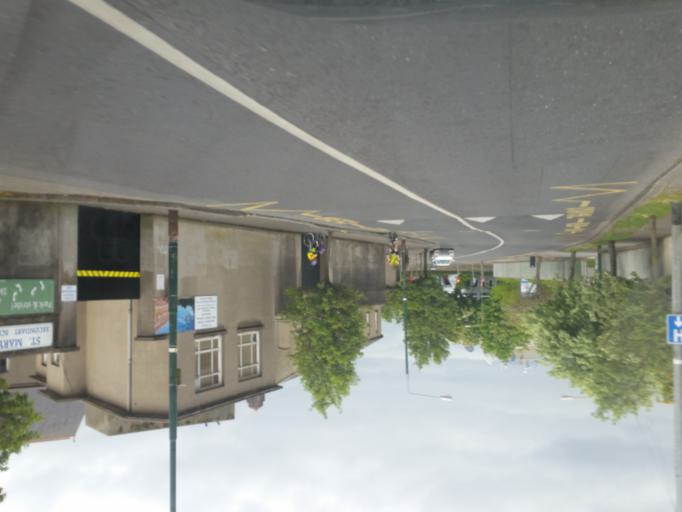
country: IE
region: Leinster
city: Glasnevin
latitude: 53.3764
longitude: -6.2721
